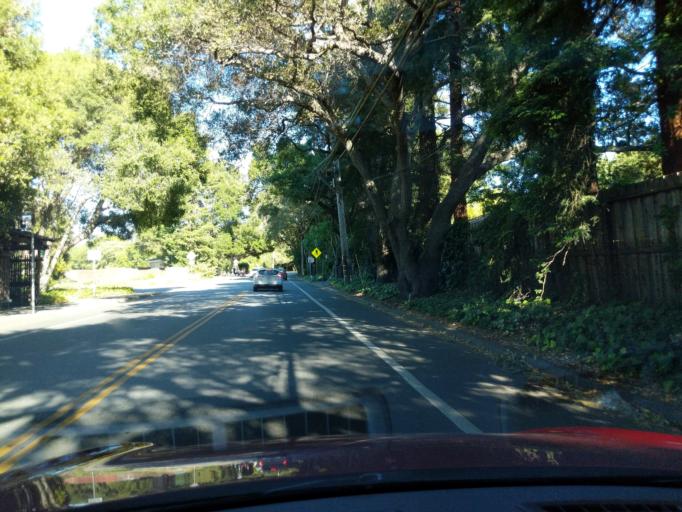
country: US
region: California
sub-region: San Mateo County
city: North Fair Oaks
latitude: 37.4756
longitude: -122.1758
